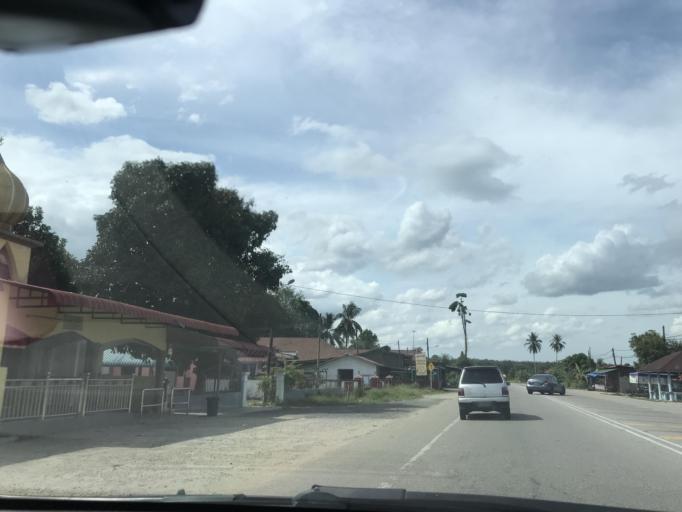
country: MY
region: Kelantan
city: Tanah Merah
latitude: 5.8543
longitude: 102.1667
